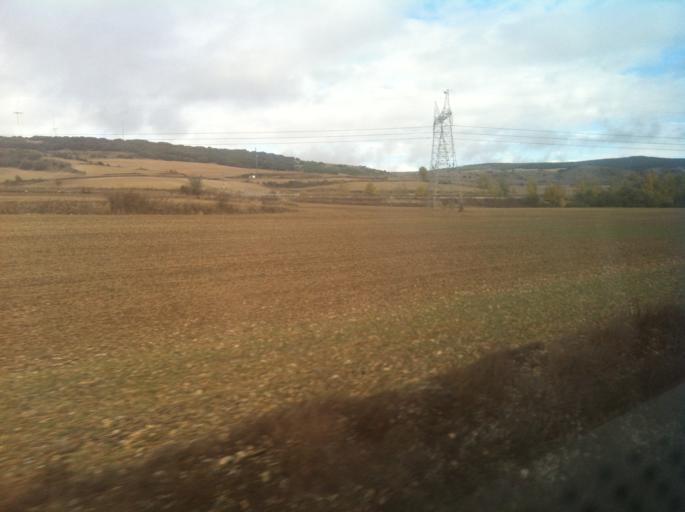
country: ES
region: Castille and Leon
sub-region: Provincia de Burgos
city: Santa Olalla de Bureba
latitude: 42.4599
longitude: -3.4497
